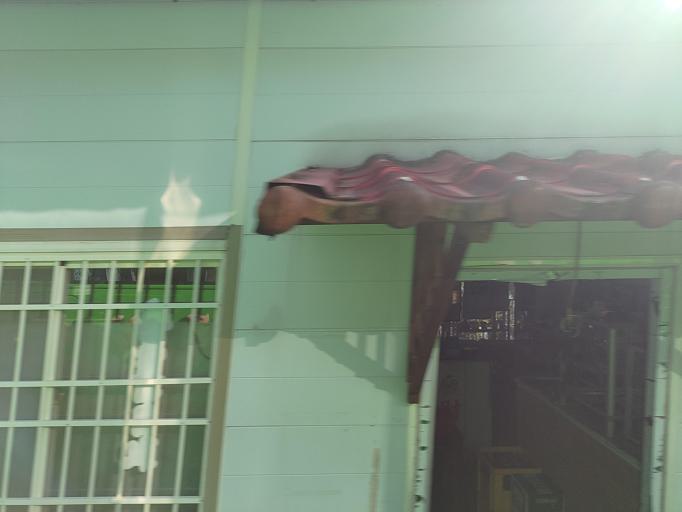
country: TW
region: Taiwan
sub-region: Hsinchu
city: Hsinchu
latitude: 24.6103
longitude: 121.0991
